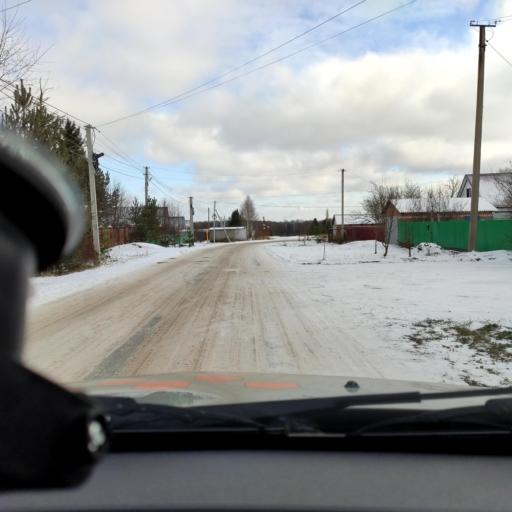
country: RU
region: Bashkortostan
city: Avdon
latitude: 54.7851
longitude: 55.7266
